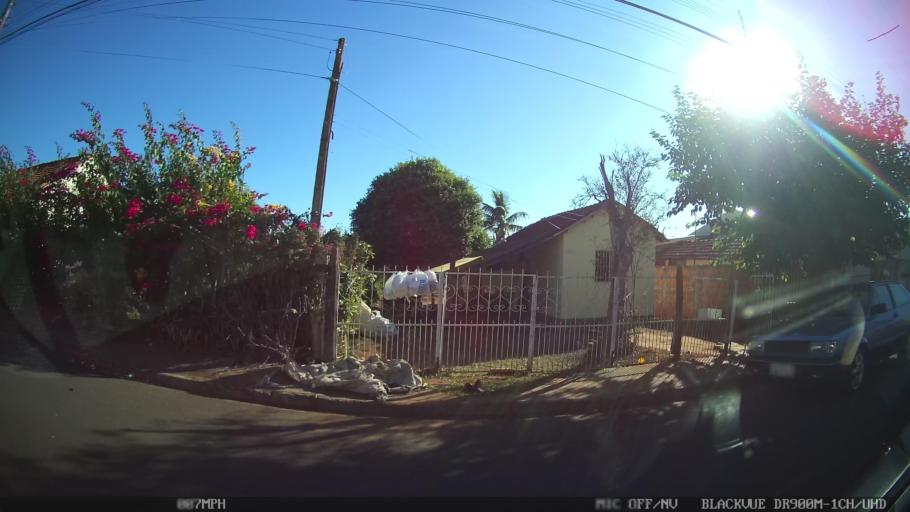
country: BR
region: Sao Paulo
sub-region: Olimpia
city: Olimpia
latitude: -20.7302
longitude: -48.9088
